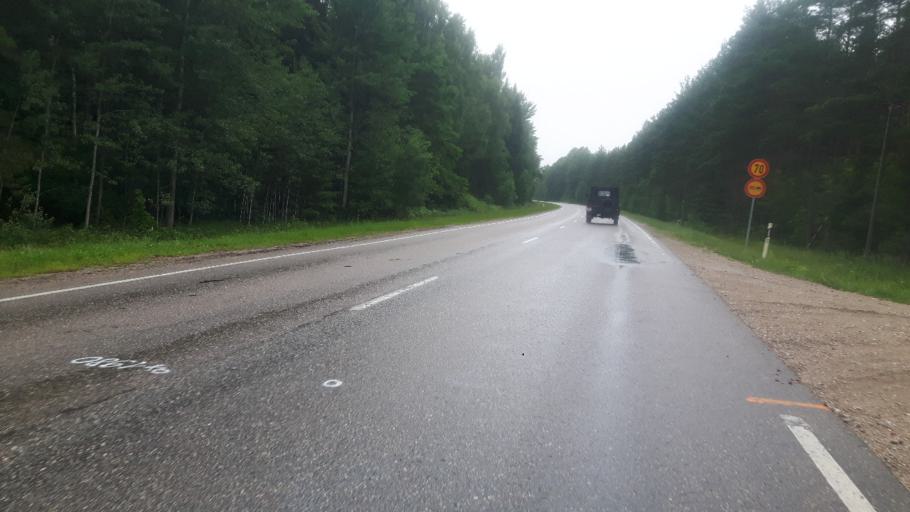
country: LV
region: Rucavas
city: Rucava
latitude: 56.1372
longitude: 21.1521
